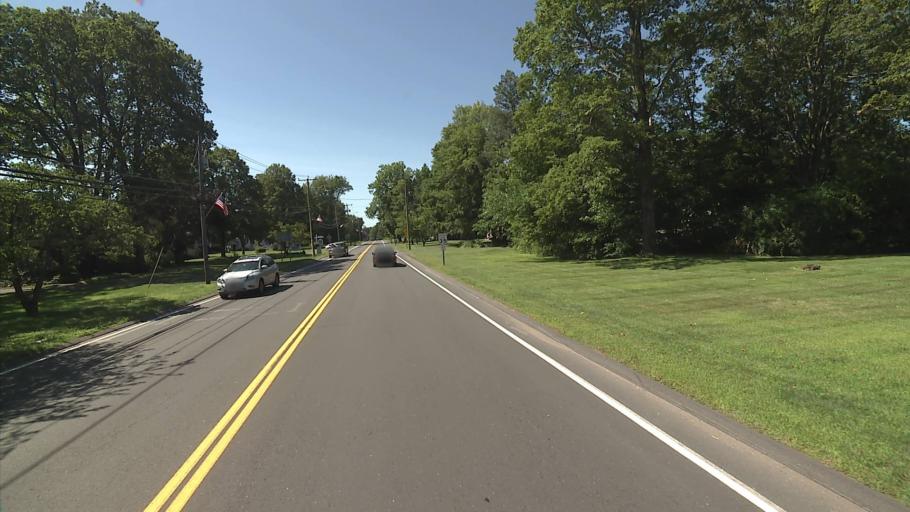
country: US
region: Connecticut
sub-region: Hartford County
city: Salmon Brook
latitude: 41.9519
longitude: -72.7896
